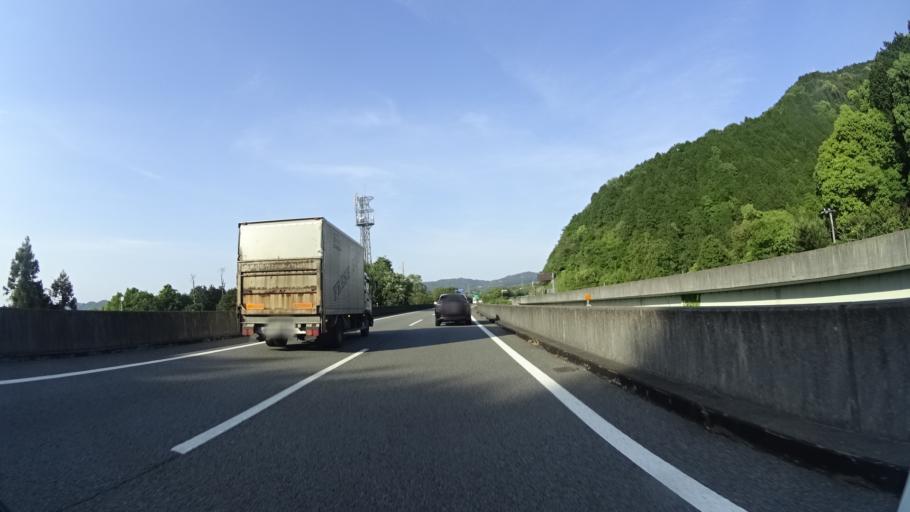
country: JP
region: Ehime
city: Niihama
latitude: 33.9229
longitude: 133.3179
